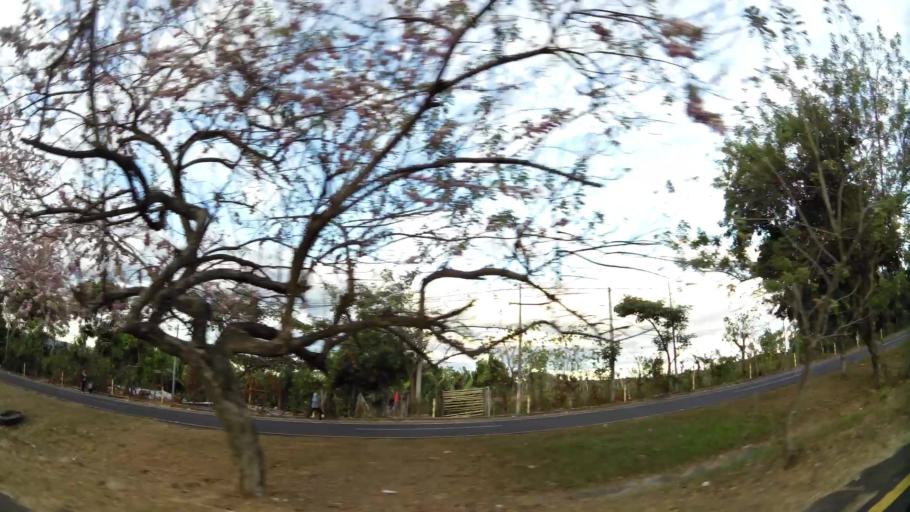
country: SV
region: San Vicente
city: San Sebastian
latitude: 13.6796
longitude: -88.8472
